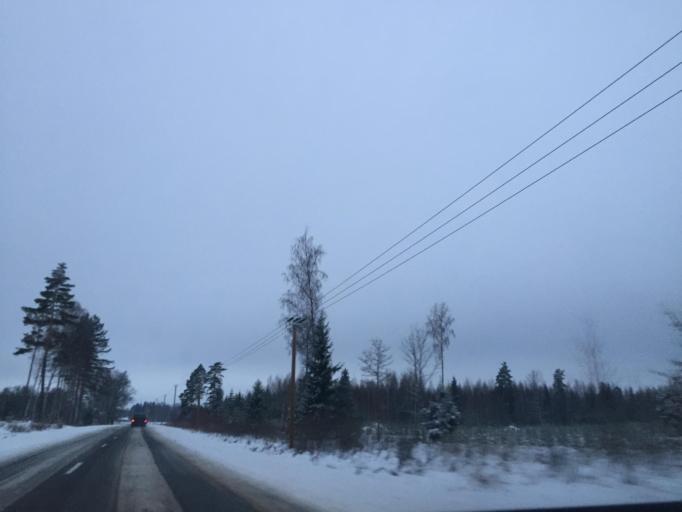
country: LV
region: Raunas
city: Rauna
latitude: 57.4357
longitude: 25.7137
